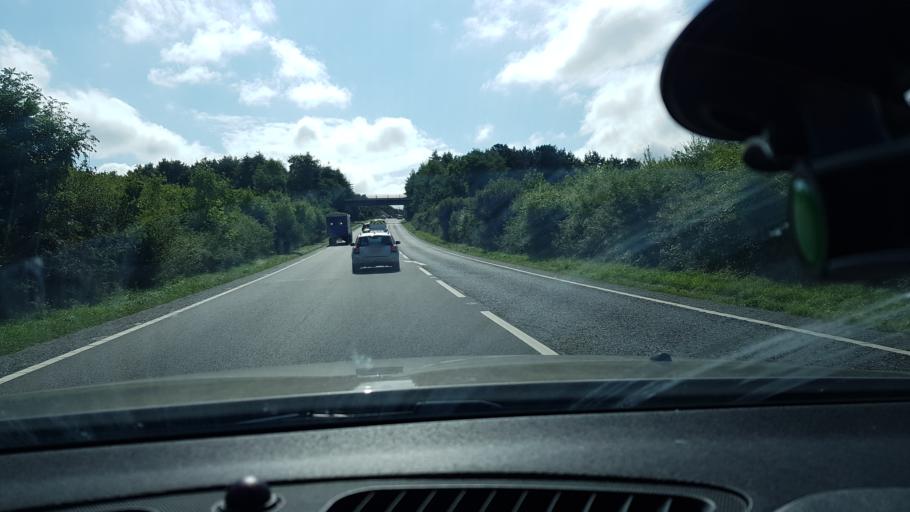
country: GB
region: England
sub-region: Cornwall
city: Truro
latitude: 50.3223
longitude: -5.0768
